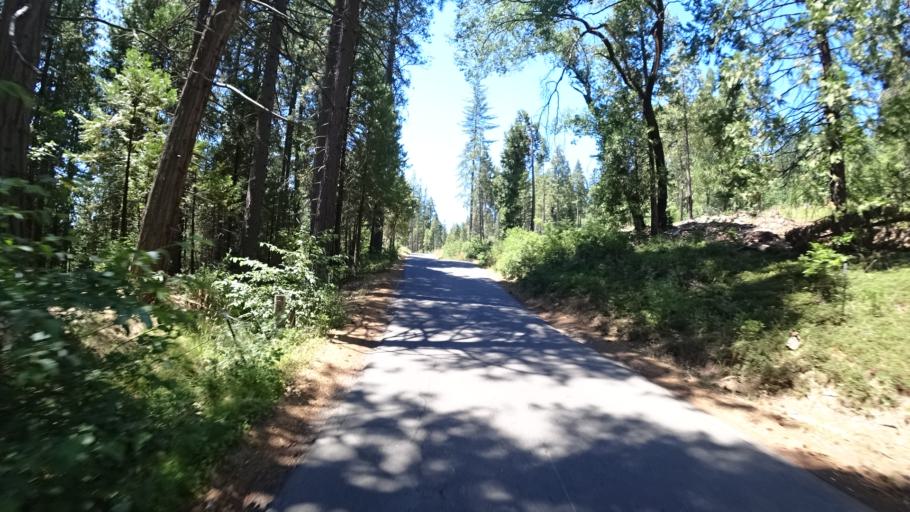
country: US
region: California
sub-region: Calaveras County
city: Arnold
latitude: 38.2143
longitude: -120.3609
